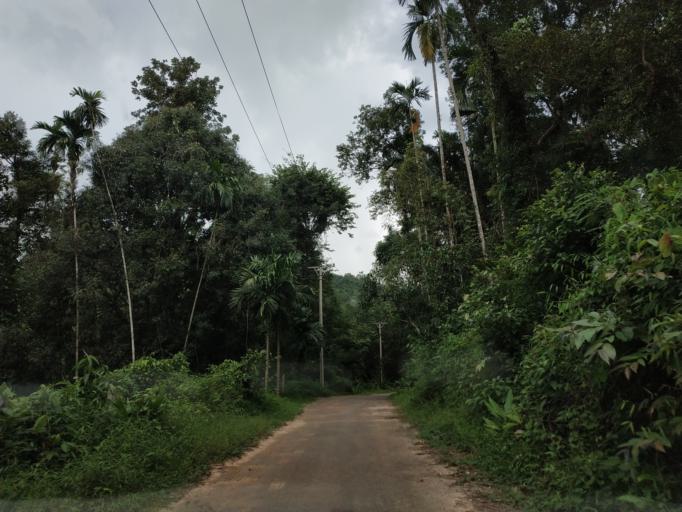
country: MM
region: Tanintharyi
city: Dawei
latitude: 13.8632
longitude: 98.2718
